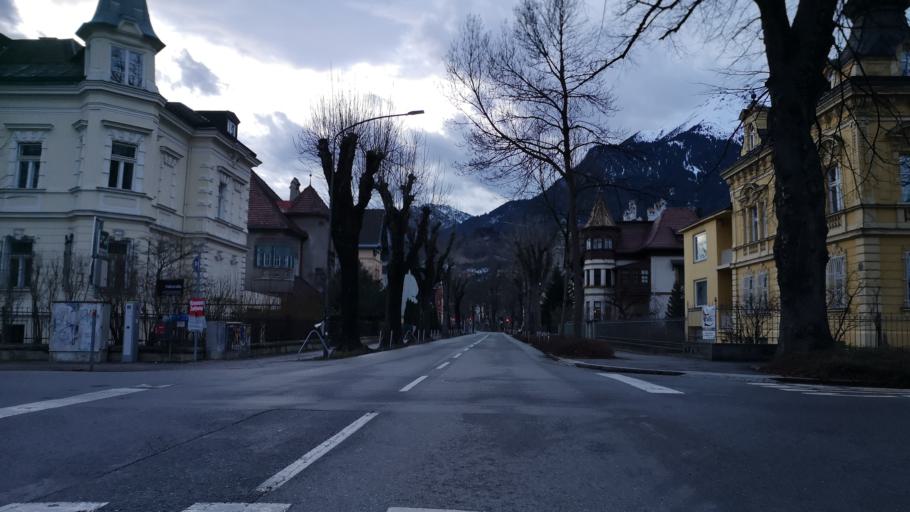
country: AT
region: Tyrol
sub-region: Innsbruck Stadt
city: Innsbruck
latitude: 47.2739
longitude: 11.4030
